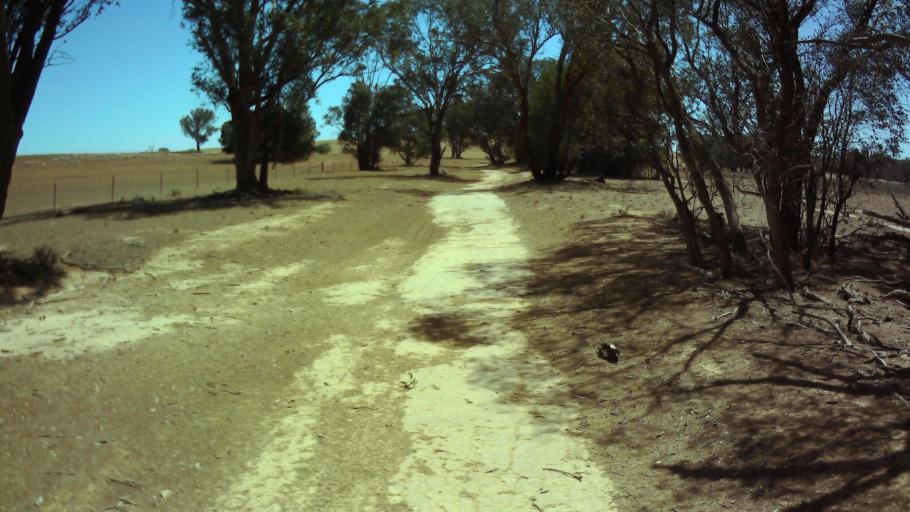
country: AU
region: New South Wales
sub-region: Weddin
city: Grenfell
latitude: -33.9847
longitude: 148.1641
